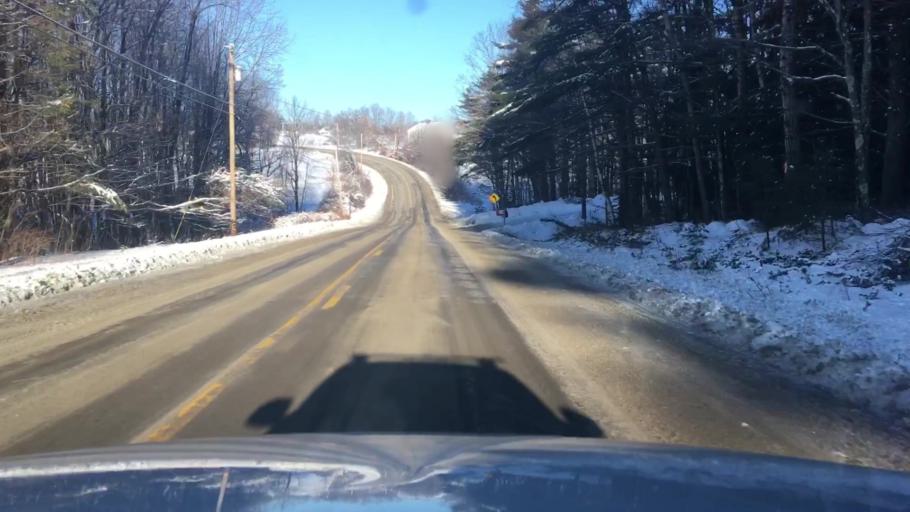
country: US
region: Maine
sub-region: Kennebec County
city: Readfield
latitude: 44.4281
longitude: -69.9360
